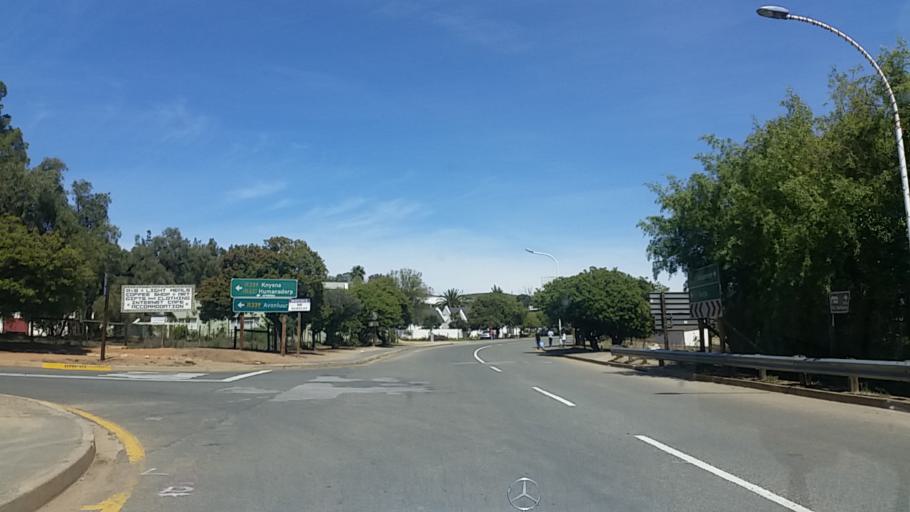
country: ZA
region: Western Cape
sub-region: Eden District Municipality
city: Knysna
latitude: -33.6584
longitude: 23.1237
